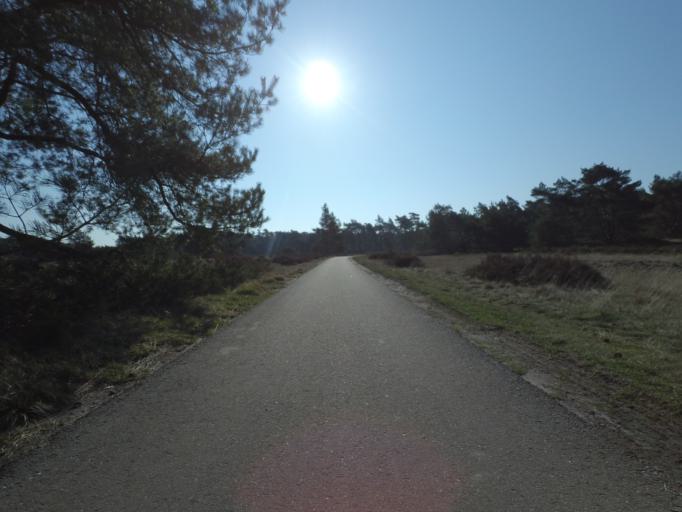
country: NL
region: Gelderland
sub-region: Gemeente Ede
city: Otterlo
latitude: 52.0694
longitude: 5.8284
